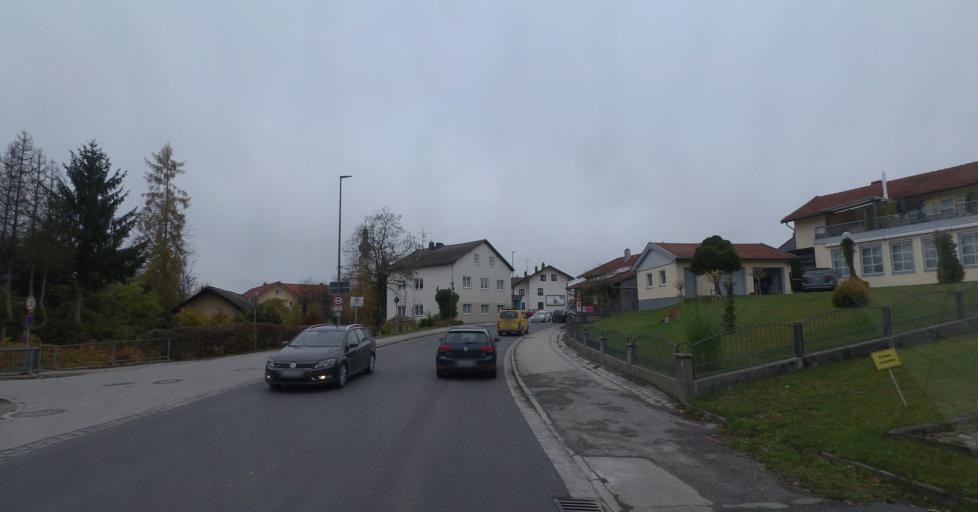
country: DE
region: Bavaria
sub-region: Upper Bavaria
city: Trostberg an der Alz
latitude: 48.0015
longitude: 12.5348
